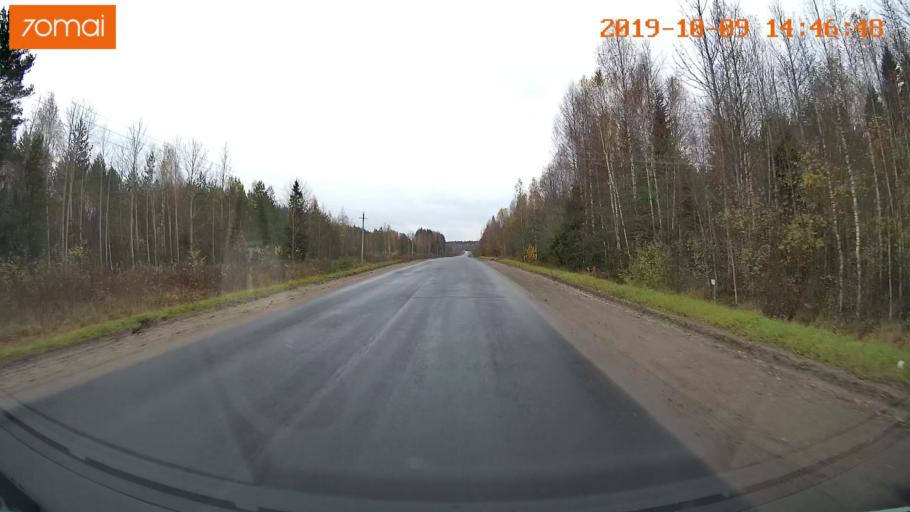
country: RU
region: Kostroma
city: Buy
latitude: 58.4264
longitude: 41.5754
